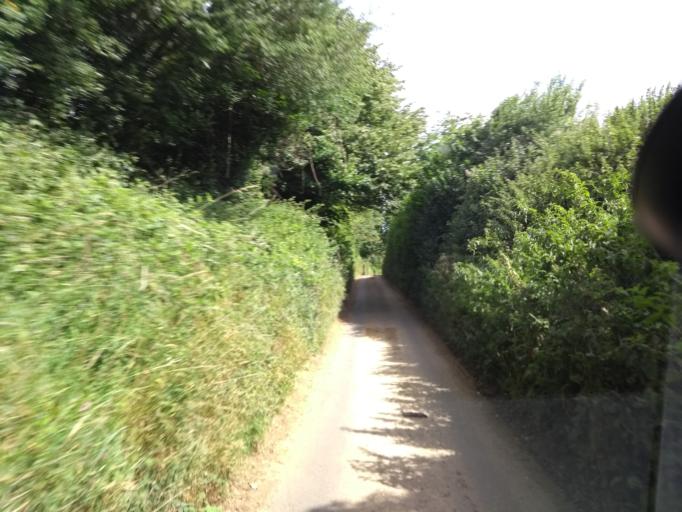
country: GB
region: England
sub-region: Somerset
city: Ilminster
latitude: 50.9226
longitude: -2.8649
